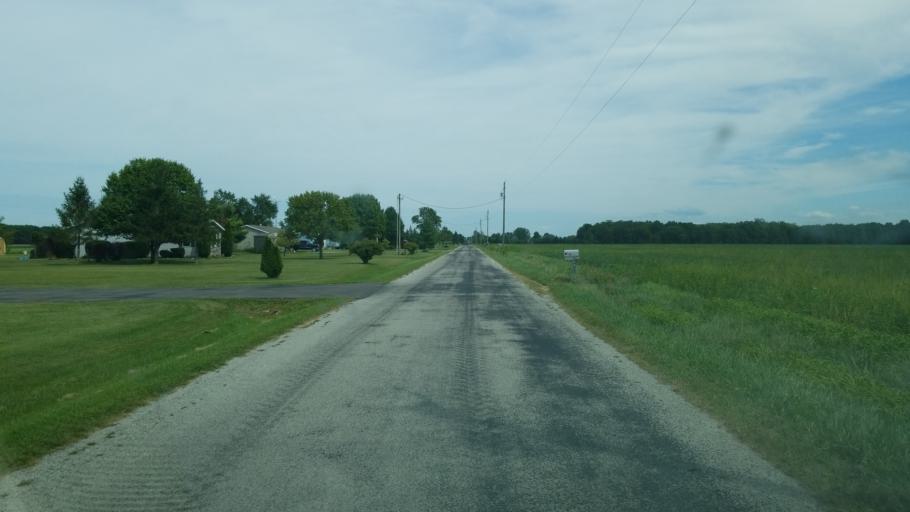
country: US
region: Ohio
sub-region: Union County
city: Richwood
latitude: 40.5932
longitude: -83.3023
